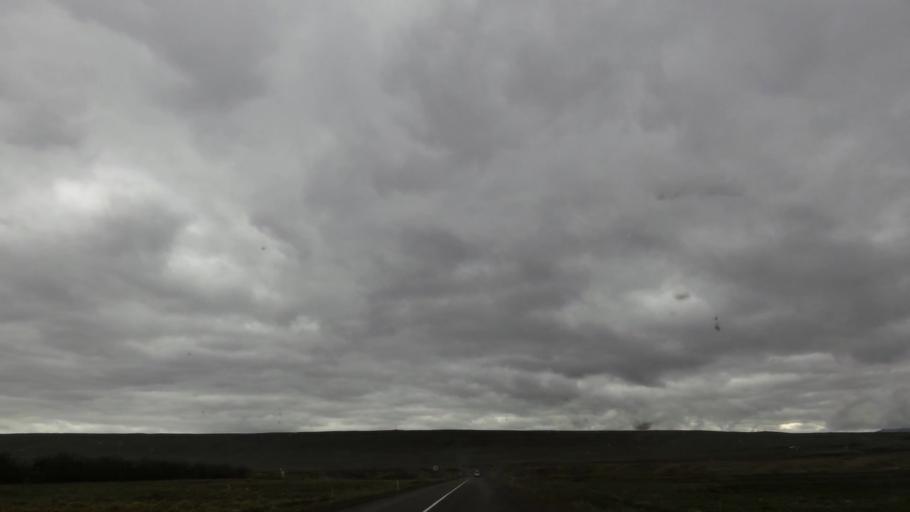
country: IS
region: West
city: Borgarnes
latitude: 65.1031
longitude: -21.7618
